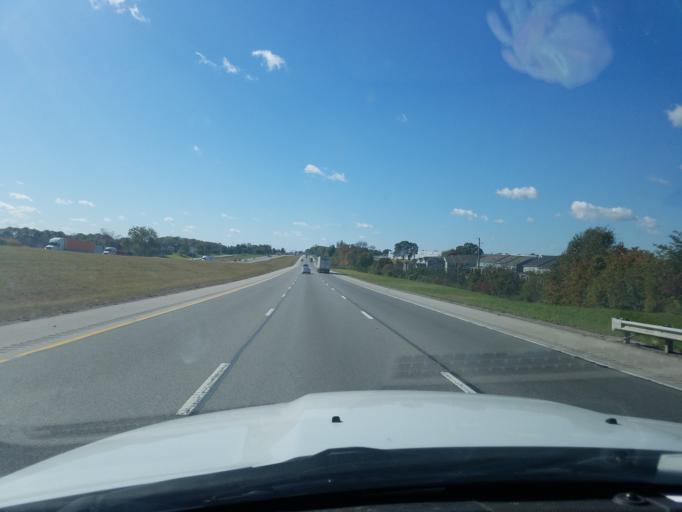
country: US
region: Kentucky
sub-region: Warren County
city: Bowling Green
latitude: 36.9604
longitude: -86.4012
